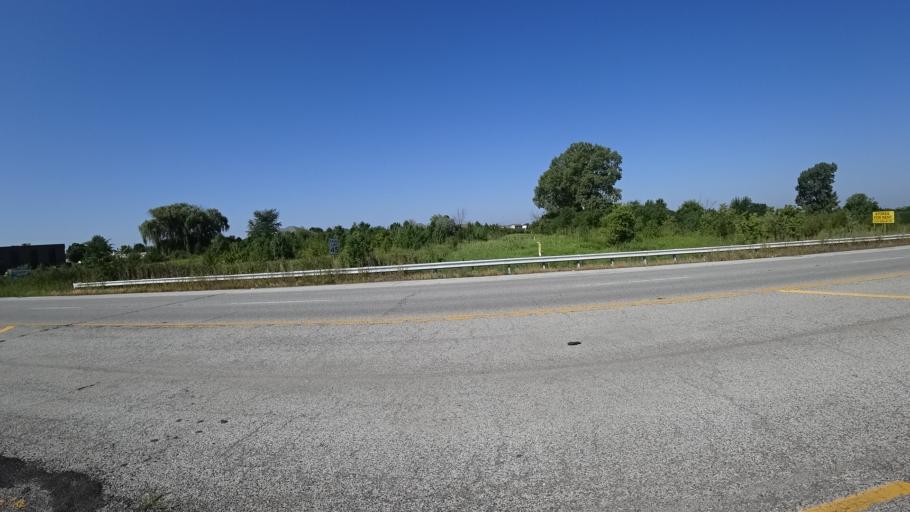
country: US
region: Illinois
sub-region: Will County
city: Frankfort Square
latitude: 41.5388
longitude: -87.7904
